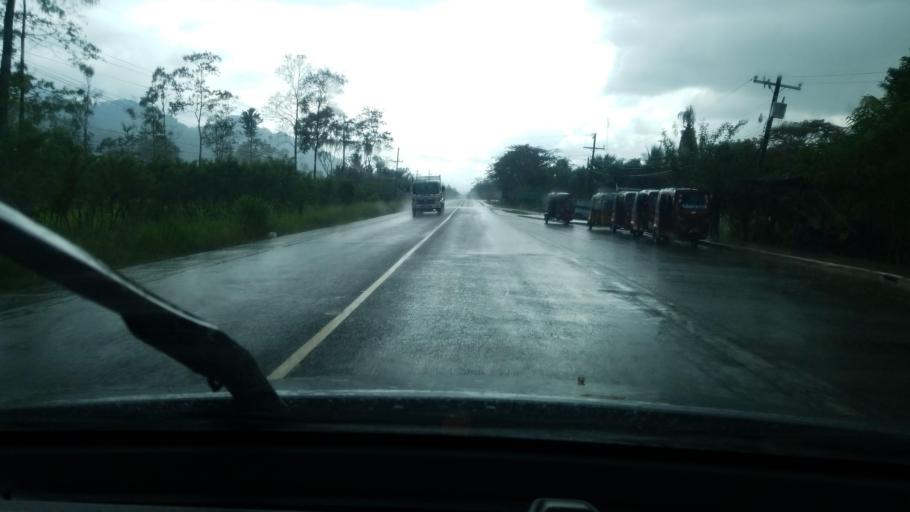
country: HN
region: Cortes
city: Rio Chiquito
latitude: 15.6291
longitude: -88.2522
